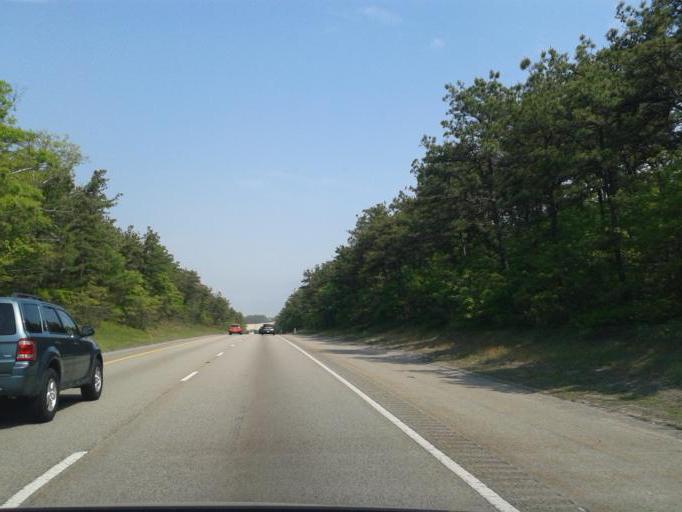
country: US
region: Massachusetts
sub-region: Barnstable County
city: Sagamore
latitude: 41.8215
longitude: -70.5572
